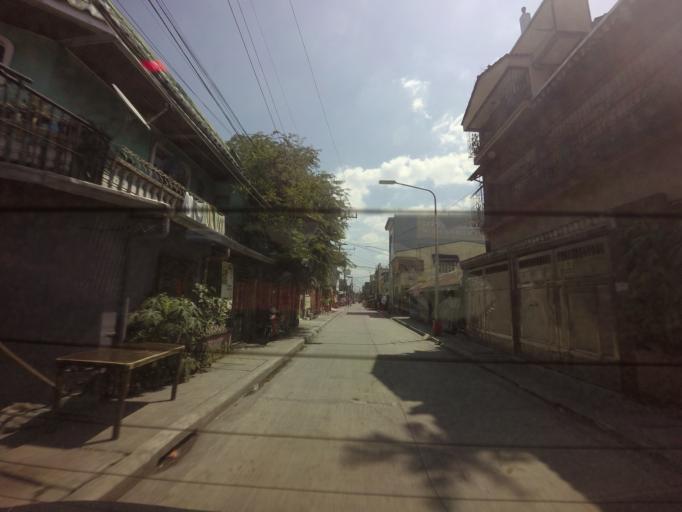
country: PH
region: Metro Manila
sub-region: Caloocan City
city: Niugan
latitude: 14.6483
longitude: 120.9581
